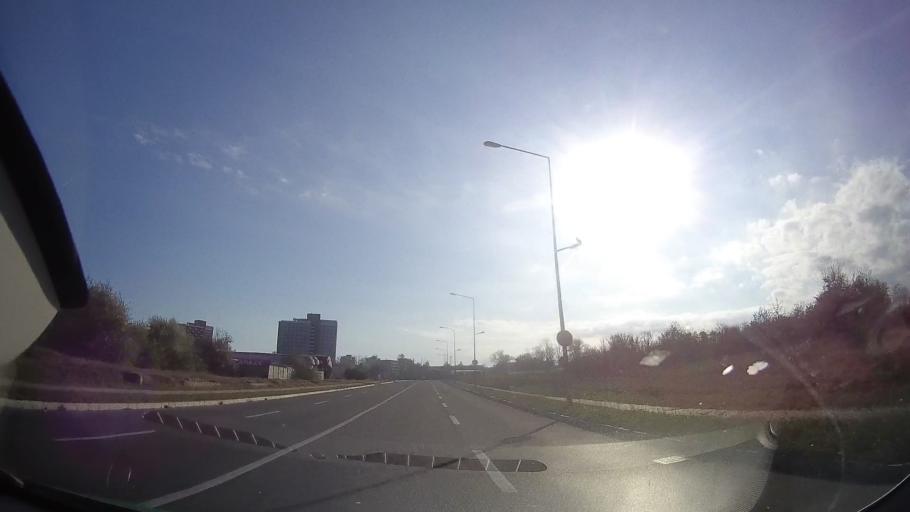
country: RO
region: Constanta
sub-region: Municipiul Mangalia
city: Mangalia
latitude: 43.8345
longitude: 28.5887
